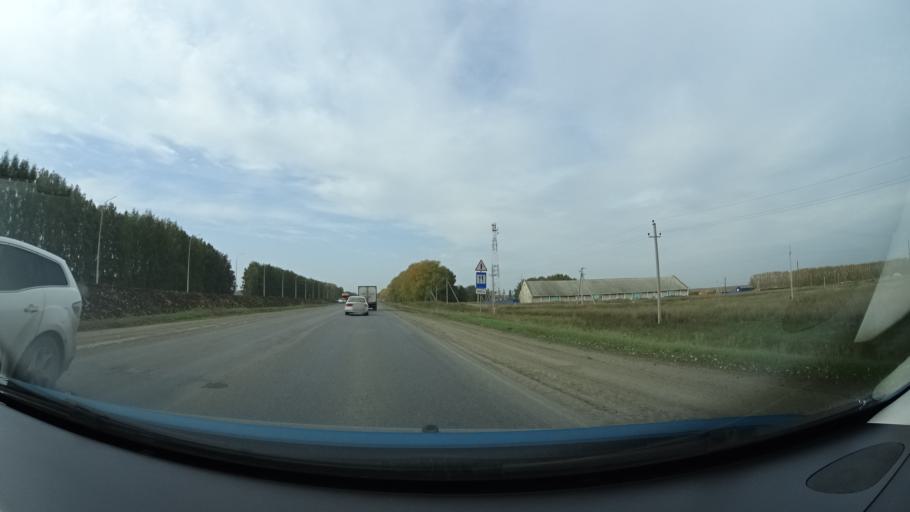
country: RU
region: Bashkortostan
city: Buzdyak
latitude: 54.6483
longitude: 54.5840
